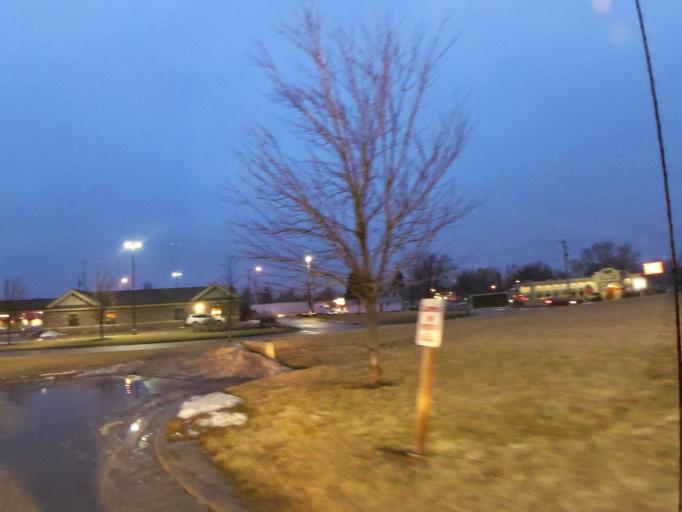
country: US
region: Illinois
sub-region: McLean County
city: Le Roy
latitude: 40.3409
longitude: -88.7608
